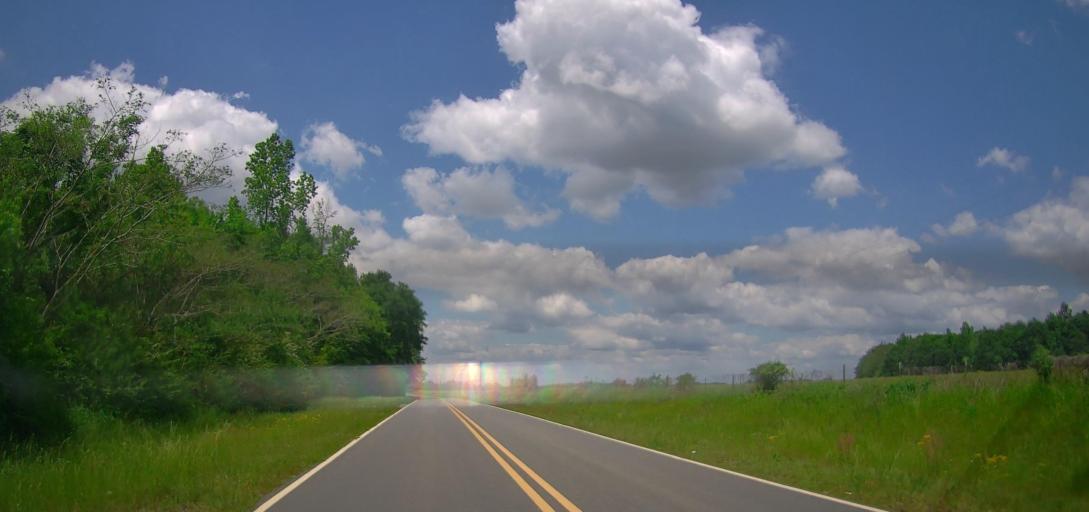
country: US
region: Georgia
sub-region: Laurens County
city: East Dublin
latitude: 32.6292
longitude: -82.8348
